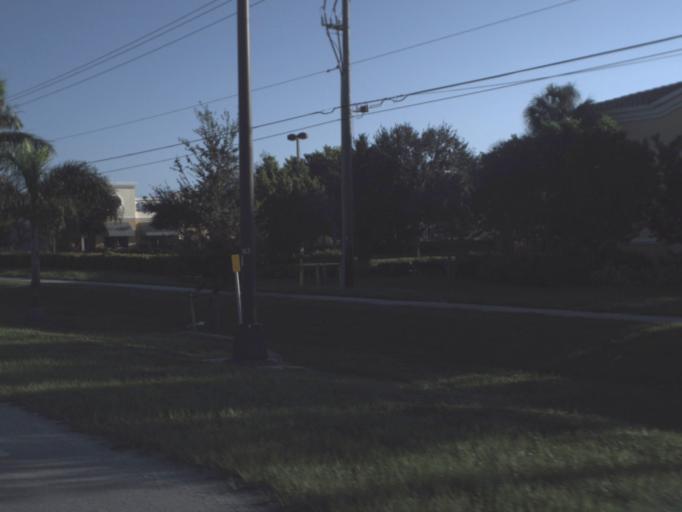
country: US
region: Florida
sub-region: Lee County
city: Bonita Springs
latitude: 26.3709
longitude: -81.8077
